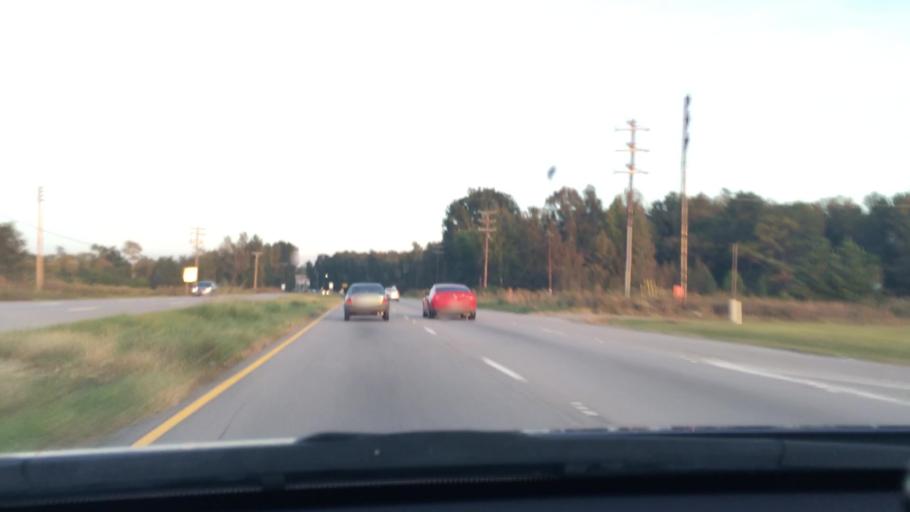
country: US
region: South Carolina
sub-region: Richland County
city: Hopkins
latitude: 33.9444
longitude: -80.8813
